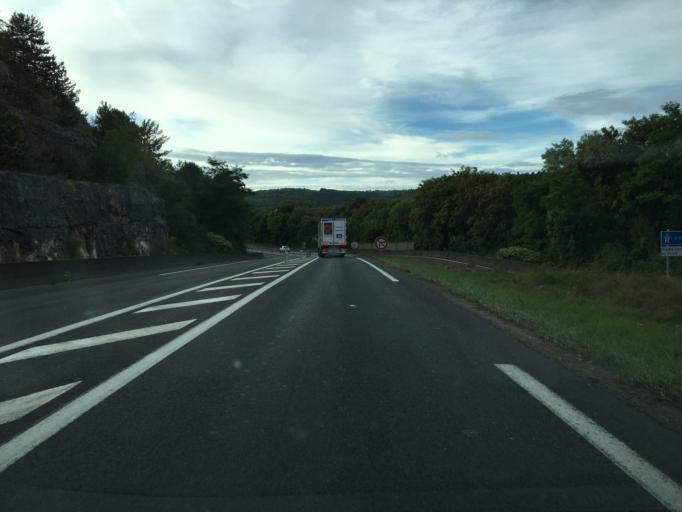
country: FR
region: Bourgogne
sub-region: Departement de la Cote-d'Or
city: Plombieres-les-Dijon
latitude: 47.3330
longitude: 4.9773
